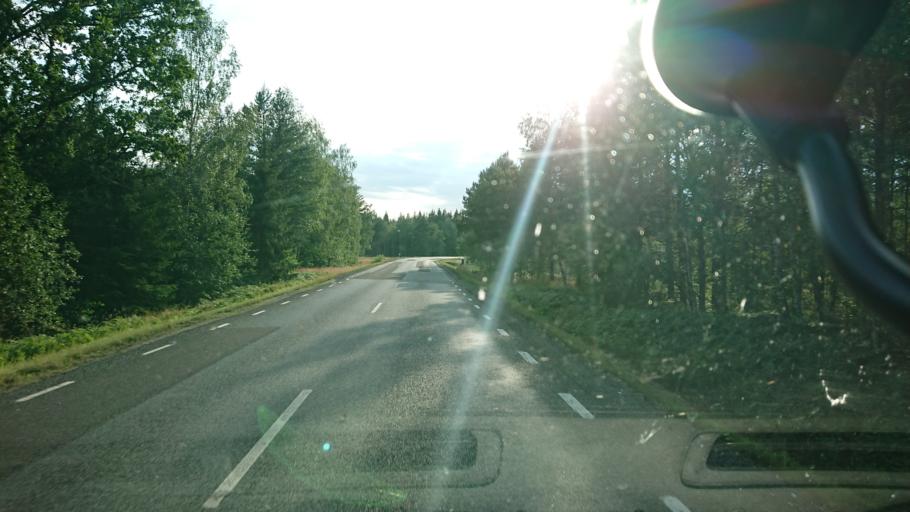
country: SE
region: Kronoberg
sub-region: Vaxjo Kommun
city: Rottne
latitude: 57.0333
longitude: 14.9541
